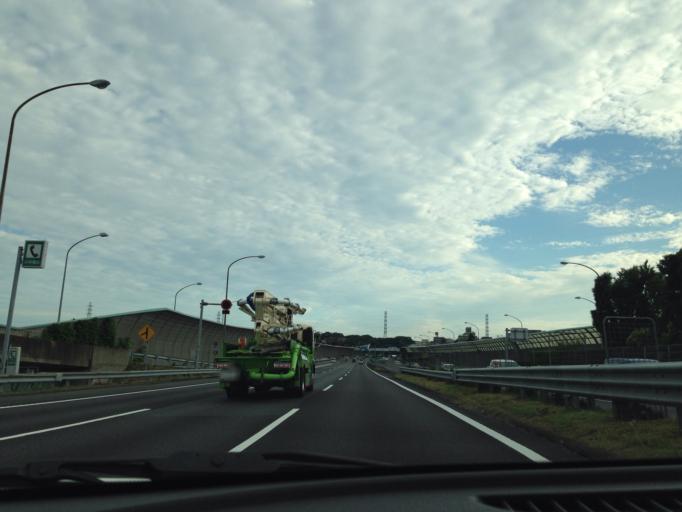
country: JP
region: Tokyo
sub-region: Machida-shi
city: Machida
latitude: 35.5419
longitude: 139.5385
